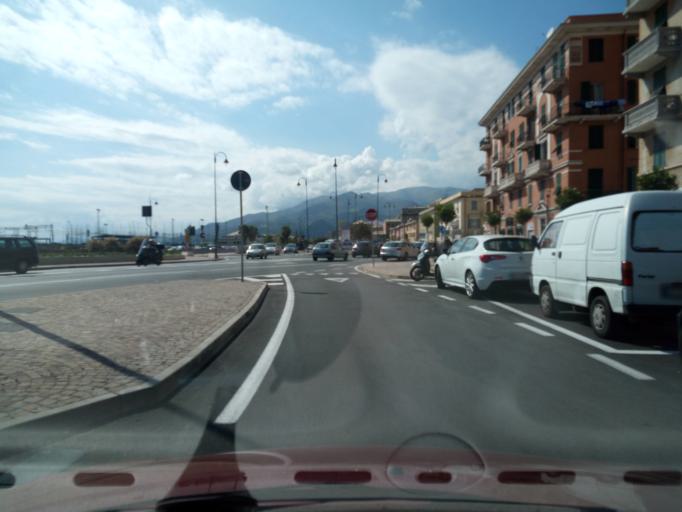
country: IT
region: Liguria
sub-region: Provincia di Genova
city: Mele
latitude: 44.4268
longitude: 8.7880
